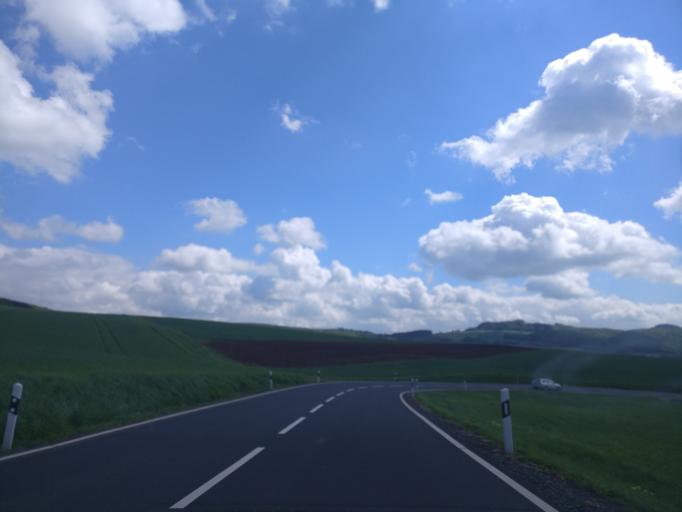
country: DE
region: Lower Saxony
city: Scheden
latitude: 51.4679
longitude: 9.7207
